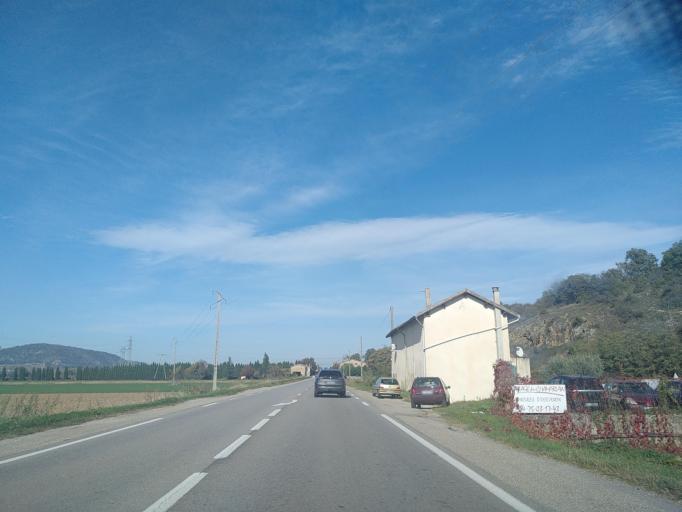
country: FR
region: Rhone-Alpes
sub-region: Departement de la Drome
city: Beausemblant
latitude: 45.2135
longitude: 4.8157
